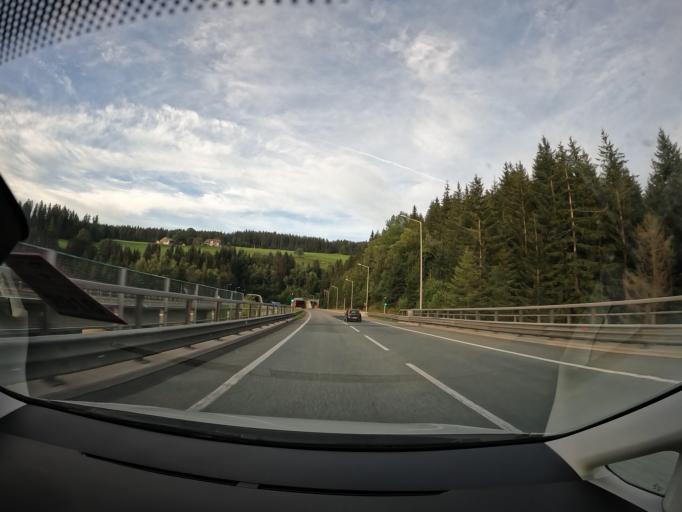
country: AT
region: Styria
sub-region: Politischer Bezirk Voitsberg
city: Pack
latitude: 46.9439
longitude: 15.0036
